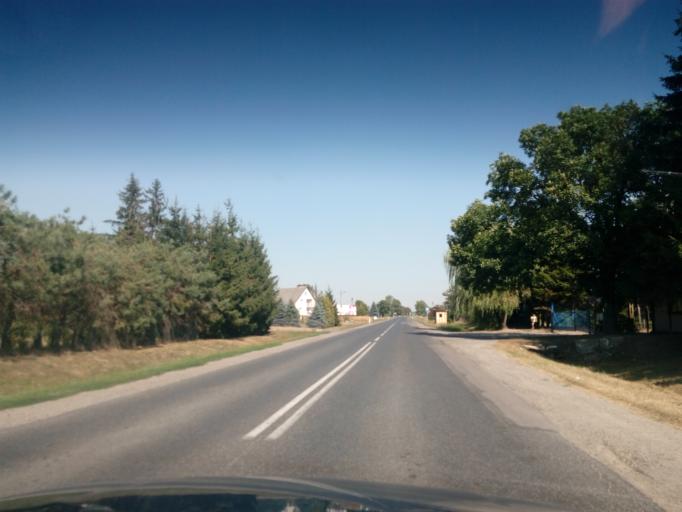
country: PL
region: Lublin Voivodeship
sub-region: Powiat hrubieszowski
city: Hrubieszow
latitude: 50.8215
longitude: 23.9396
